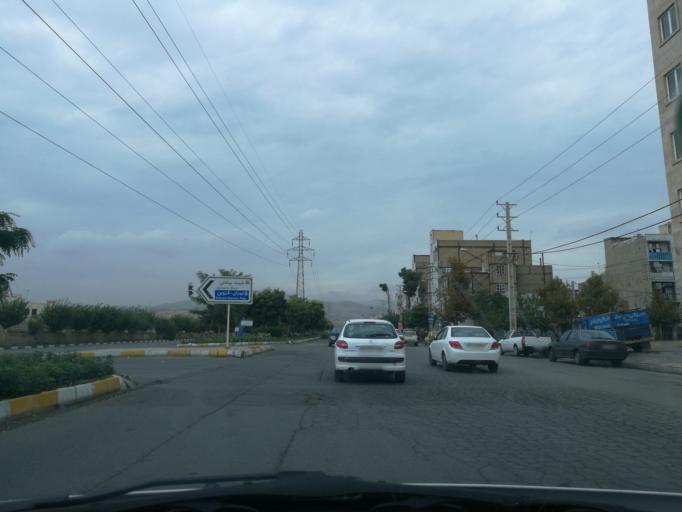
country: IR
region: Alborz
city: Karaj
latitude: 35.8534
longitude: 50.9197
